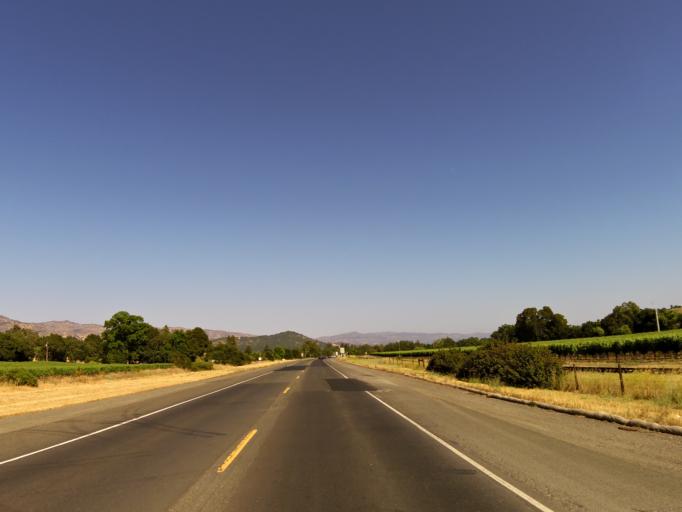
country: US
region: California
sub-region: Napa County
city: Yountville
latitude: 38.4092
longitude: -122.3761
